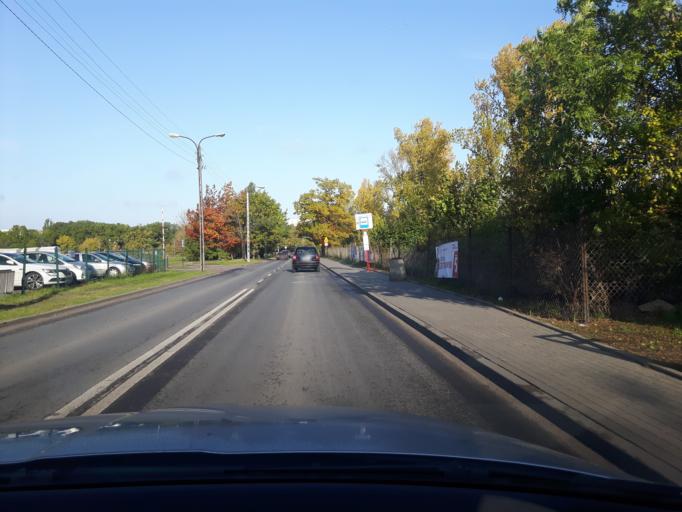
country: PL
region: Masovian Voivodeship
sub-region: Warszawa
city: Targowek
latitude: 52.2836
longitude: 21.0526
